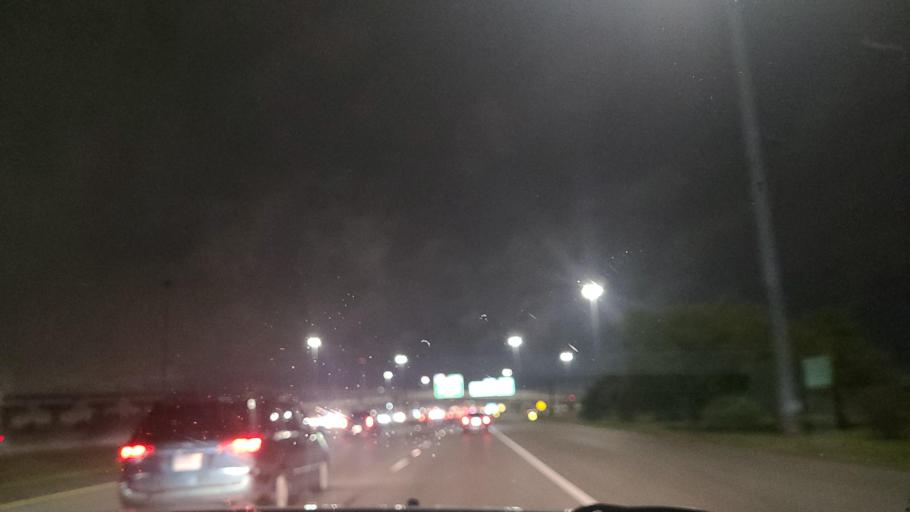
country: US
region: Texas
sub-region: Tarrant County
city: Arlington
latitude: 32.6772
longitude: -97.0682
